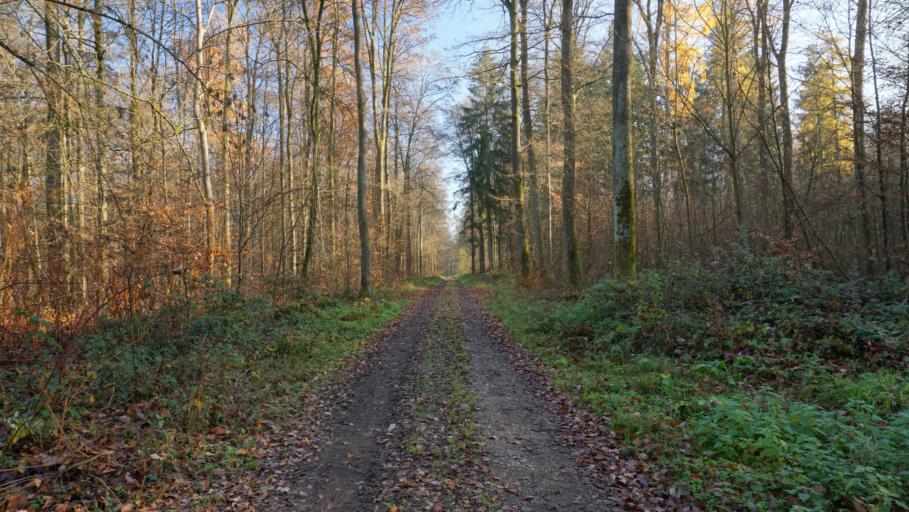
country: DE
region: Baden-Wuerttemberg
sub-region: Karlsruhe Region
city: Huffenhardt
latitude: 49.3080
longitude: 9.0891
